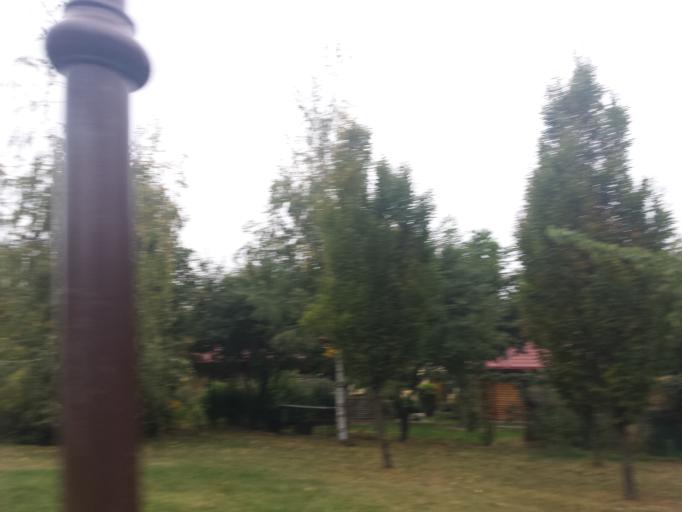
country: RO
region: Bucuresti
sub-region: Municipiul Bucuresti
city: Bucuresti
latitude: 44.4716
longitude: 26.0655
